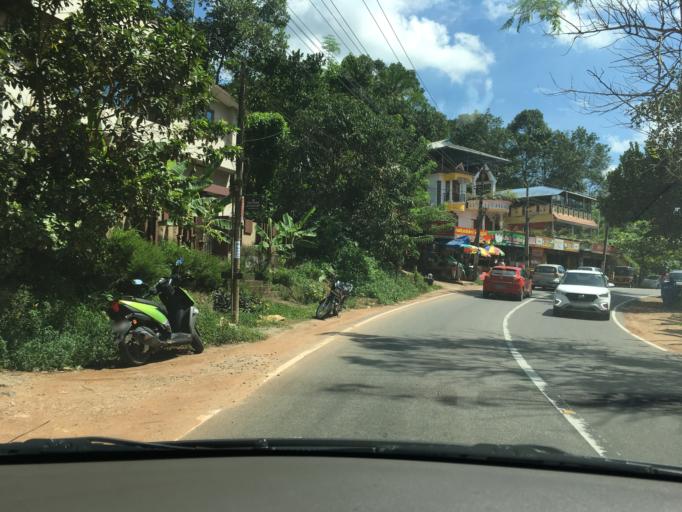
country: IN
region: Kerala
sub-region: Thiruvananthapuram
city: Nedumangad
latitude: 8.5818
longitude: 76.9951
